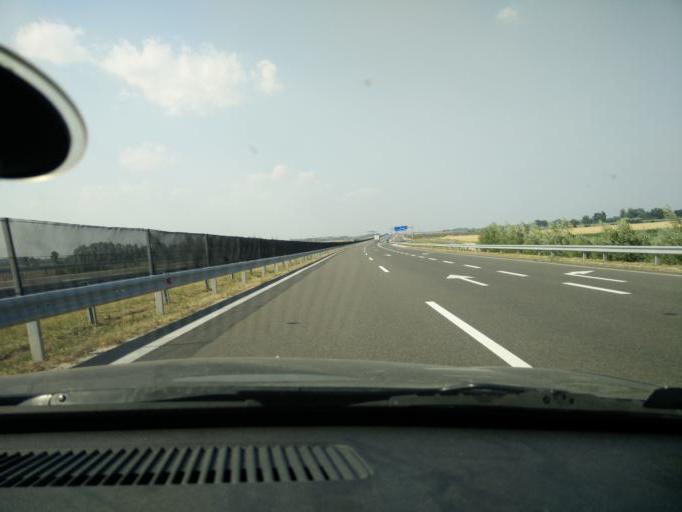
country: HU
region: Tolna
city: Szekszard
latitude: 46.3729
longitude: 18.7513
